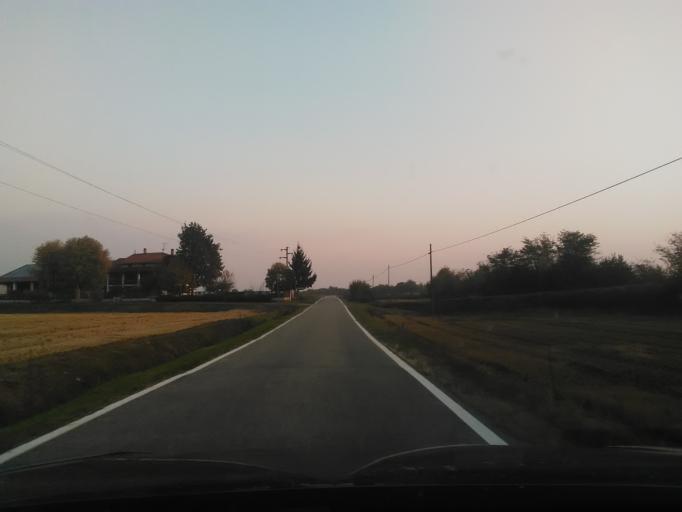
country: IT
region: Piedmont
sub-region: Provincia di Vercelli
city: Buronzo
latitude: 45.5016
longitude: 8.2889
